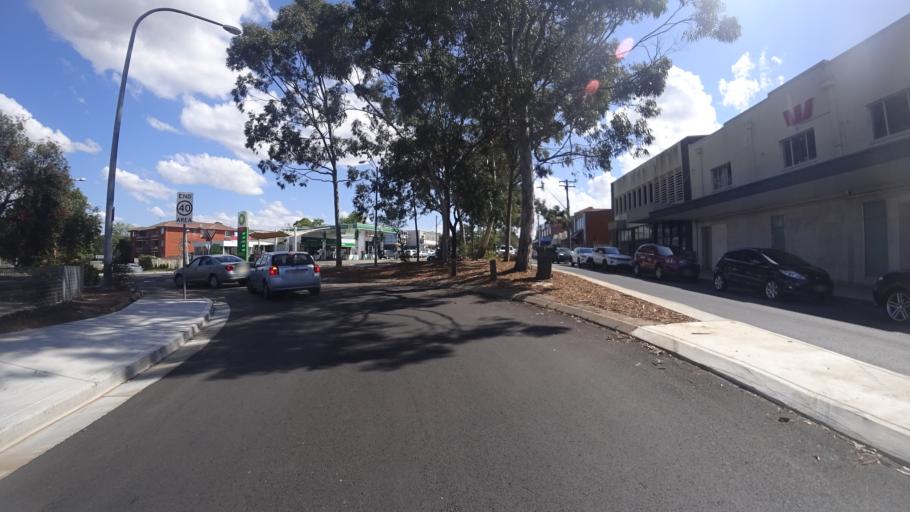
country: AU
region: New South Wales
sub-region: Fairfield
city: Liverpool
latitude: -33.8957
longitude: 150.9371
